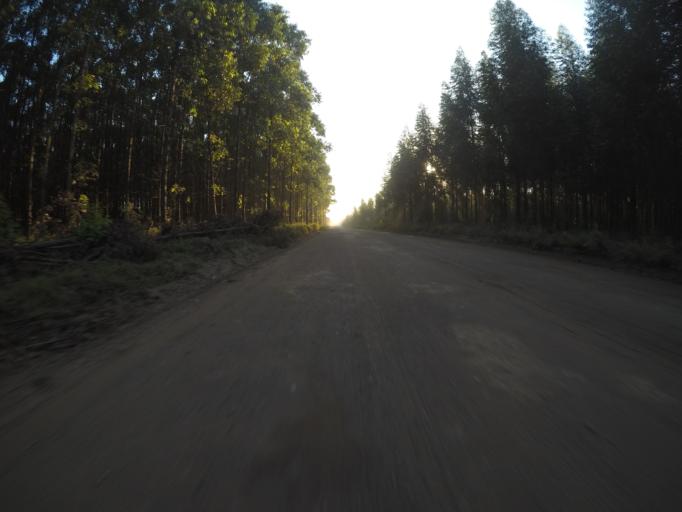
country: ZA
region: KwaZulu-Natal
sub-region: uThungulu District Municipality
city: KwaMbonambi
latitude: -28.6695
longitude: 32.0797
